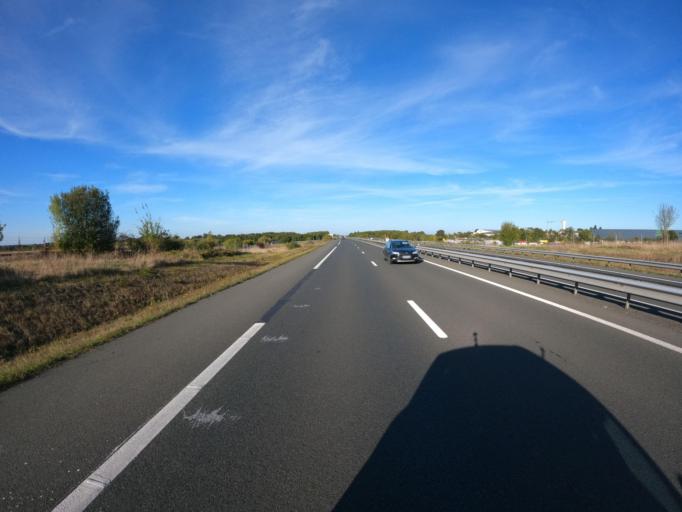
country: FR
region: Pays de la Loire
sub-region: Departement de Maine-et-Loire
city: Moze-sur-Louet
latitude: 47.3669
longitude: -0.5705
